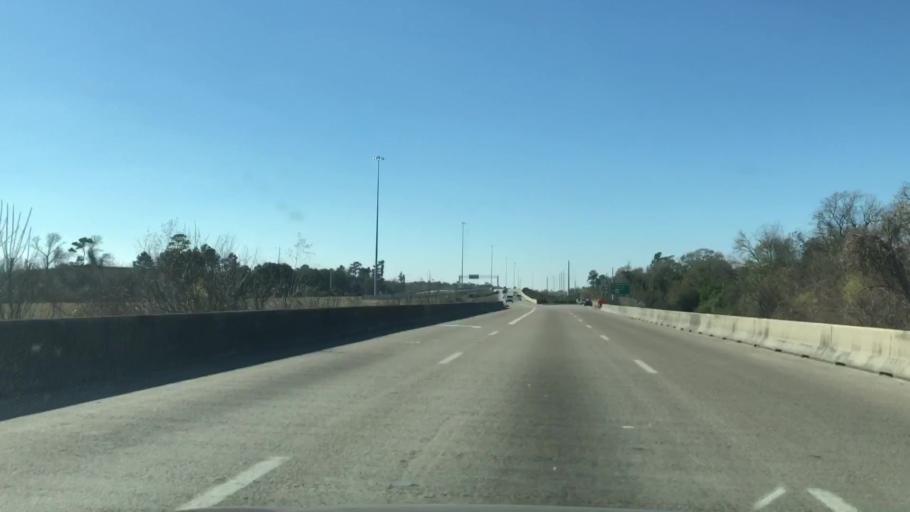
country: US
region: Texas
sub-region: Harris County
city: Jacinto City
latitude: 29.8094
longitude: -95.2142
